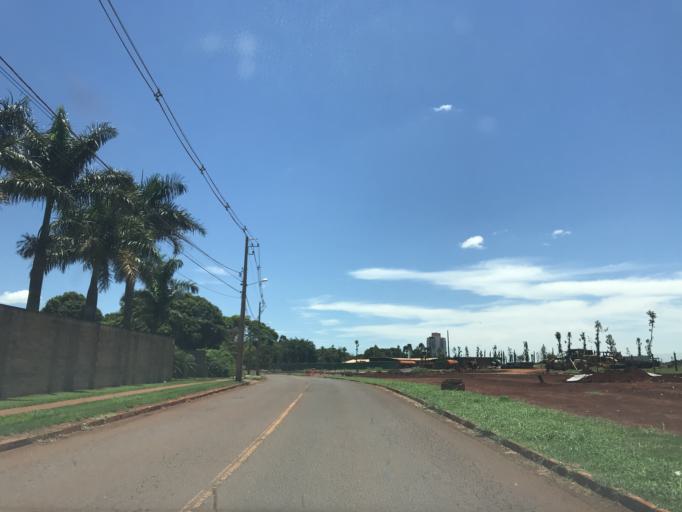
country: BR
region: Parana
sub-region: Sarandi
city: Sarandi
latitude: -23.4412
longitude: -51.9042
